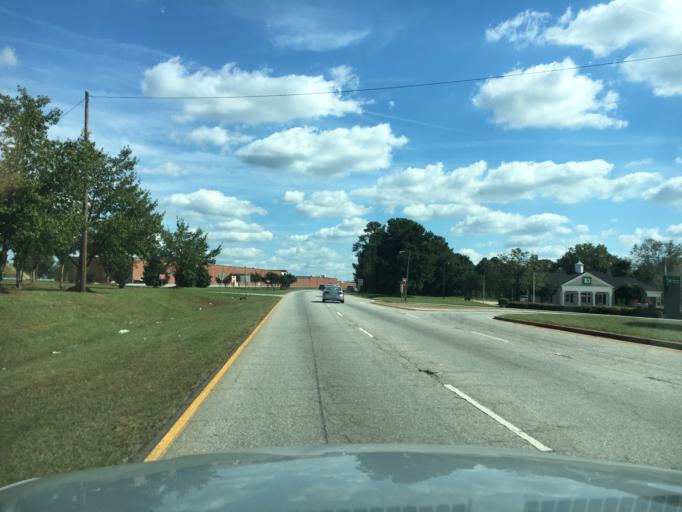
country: US
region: South Carolina
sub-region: Greenville County
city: Mauldin
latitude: 34.7737
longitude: -82.3043
